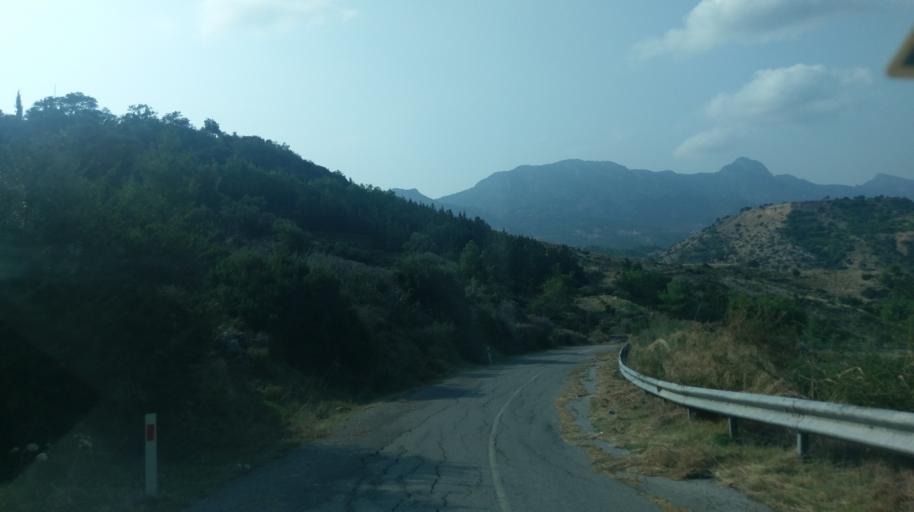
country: CY
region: Keryneia
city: Kyrenia
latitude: 35.3122
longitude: 33.4689
